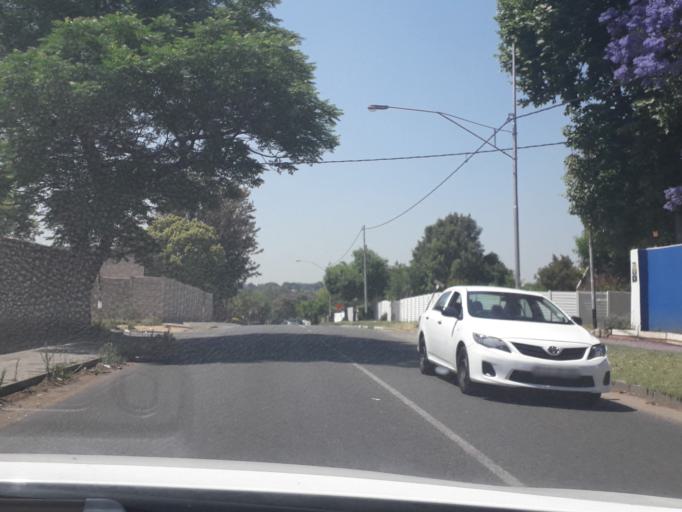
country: ZA
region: Gauteng
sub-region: City of Johannesburg Metropolitan Municipality
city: Modderfontein
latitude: -26.1288
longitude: 28.0973
